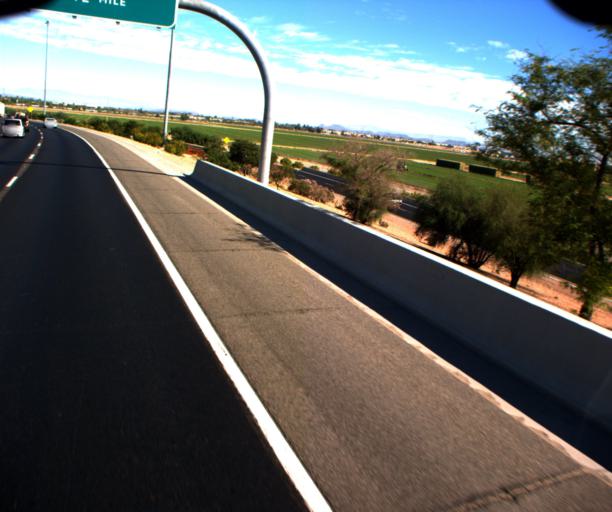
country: US
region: Arizona
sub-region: Maricopa County
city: Peoria
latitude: 33.5383
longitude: -112.2696
